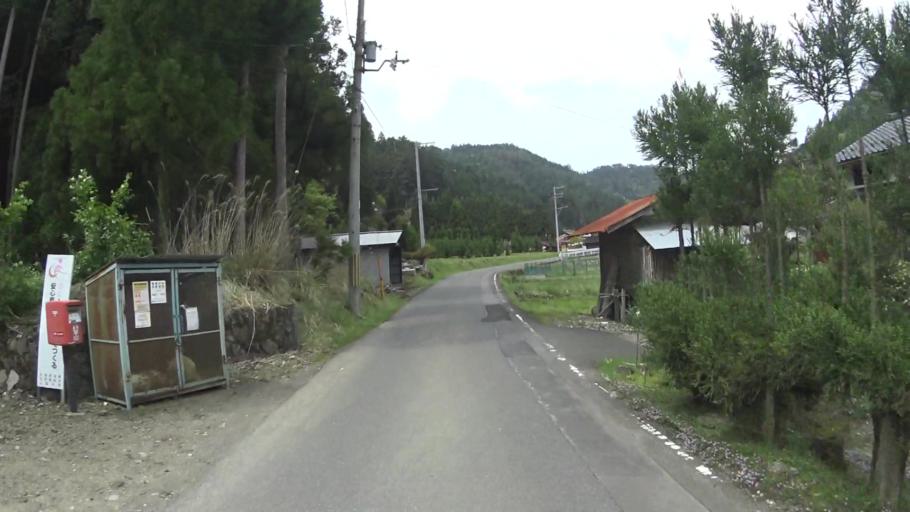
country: JP
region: Kyoto
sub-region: Kyoto-shi
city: Kamigyo-ku
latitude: 35.2113
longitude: 135.7007
